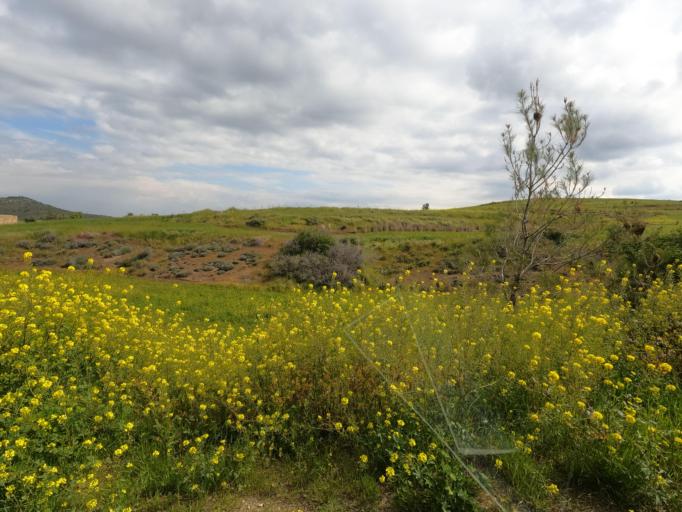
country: CY
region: Lefkosia
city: Kakopetria
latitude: 35.0764
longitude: 32.9562
